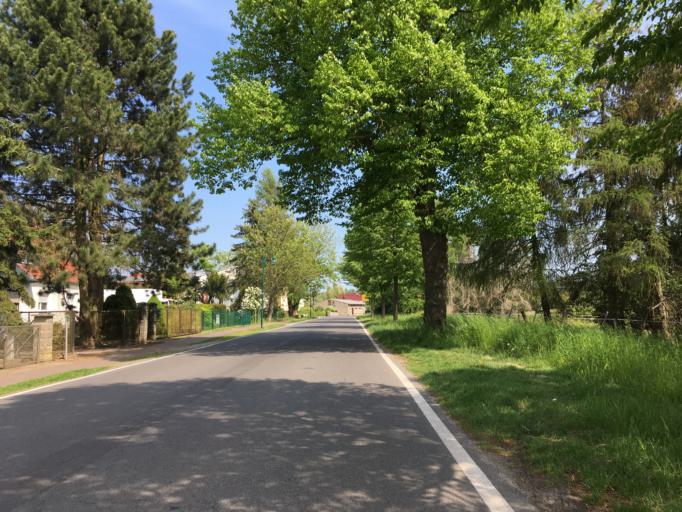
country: DE
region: Brandenburg
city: Werneuchen
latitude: 52.6791
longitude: 13.7371
